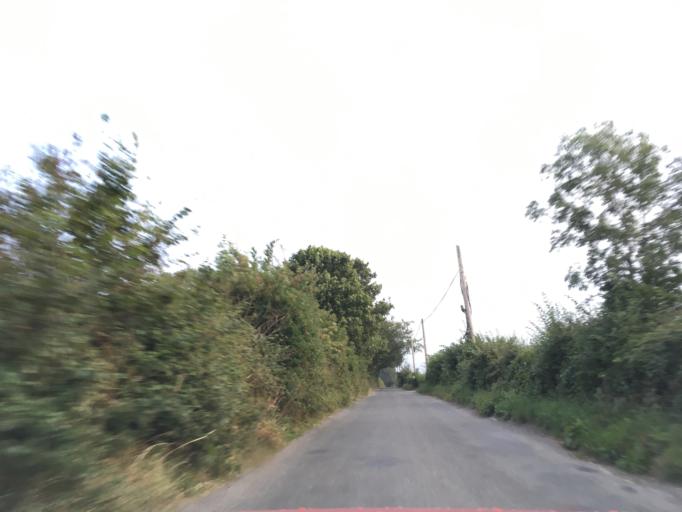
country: IE
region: Munster
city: Cashel
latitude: 52.4897
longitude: -7.9753
